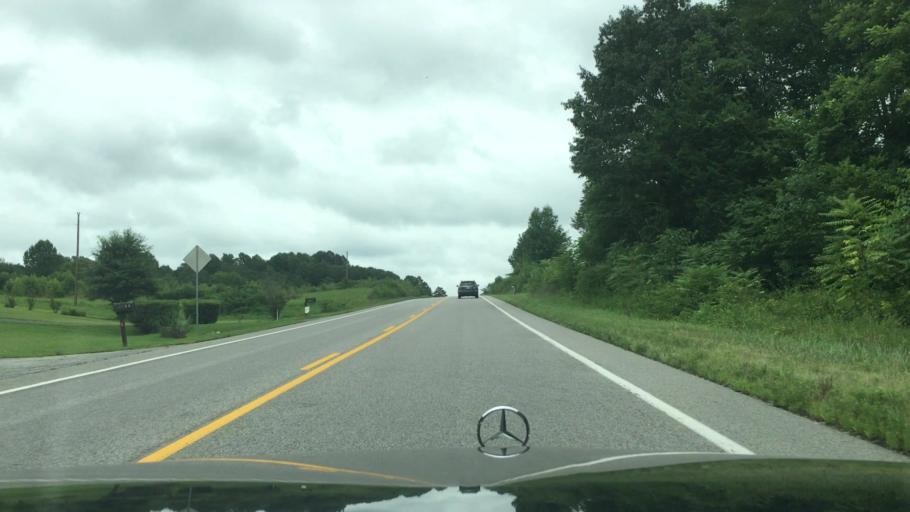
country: US
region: Virginia
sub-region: Nottoway County
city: Crewe
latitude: 37.2775
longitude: -78.2199
